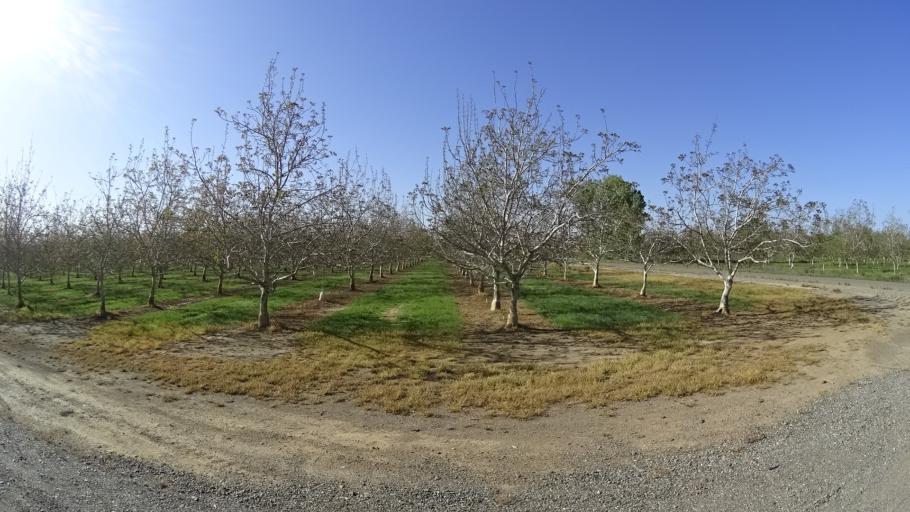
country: US
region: California
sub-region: Glenn County
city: Hamilton City
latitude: 39.6947
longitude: -122.0740
